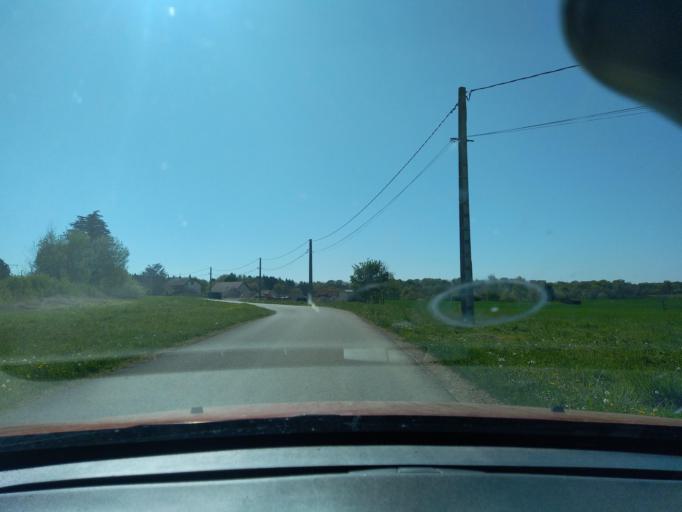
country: FR
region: Franche-Comte
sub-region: Departement du Jura
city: Cousance
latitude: 46.5808
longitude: 5.4332
